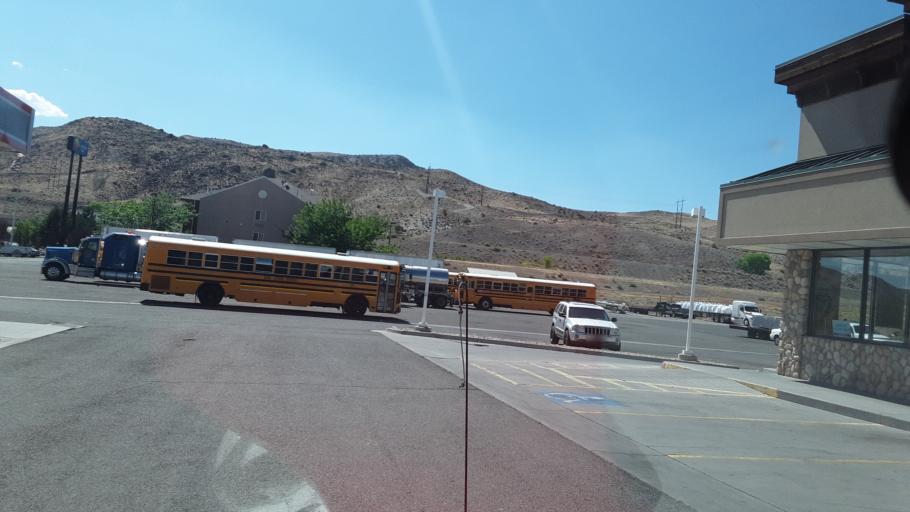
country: US
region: Utah
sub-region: Sevier County
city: Richfield
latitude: 38.7508
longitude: -112.1027
